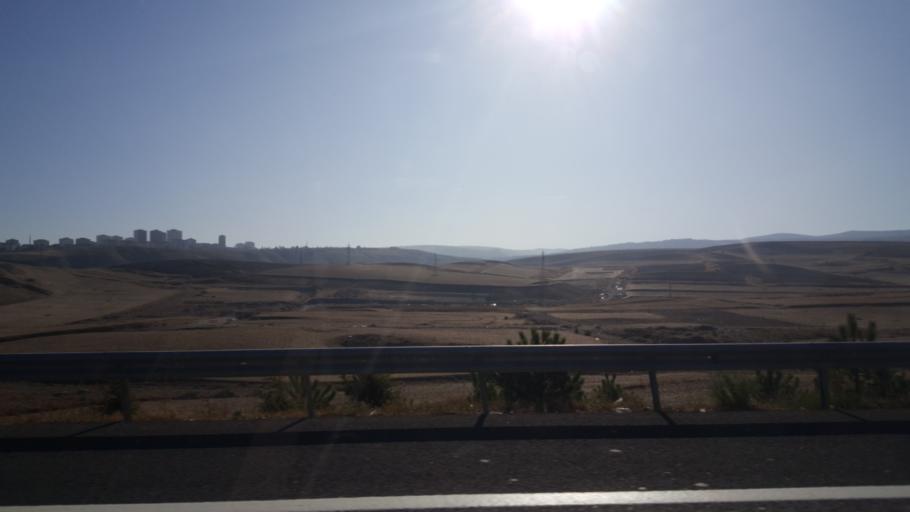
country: TR
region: Ankara
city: Mamak
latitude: 39.8920
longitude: 32.9580
